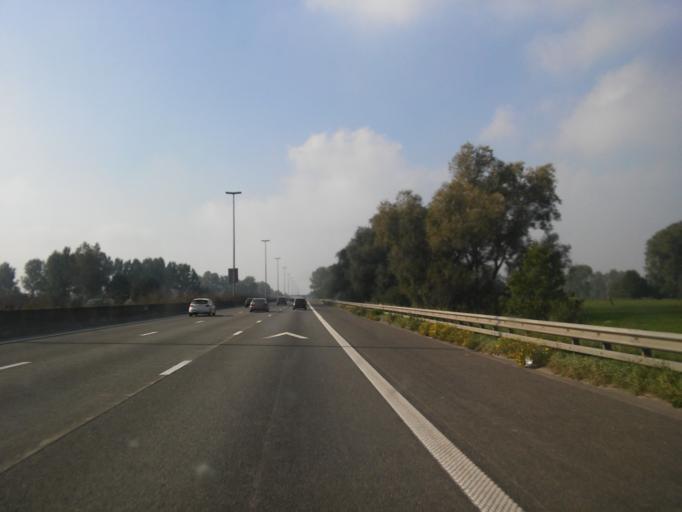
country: BE
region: Flanders
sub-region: Provincie Oost-Vlaanderen
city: Temse
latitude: 51.1566
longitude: 4.2244
